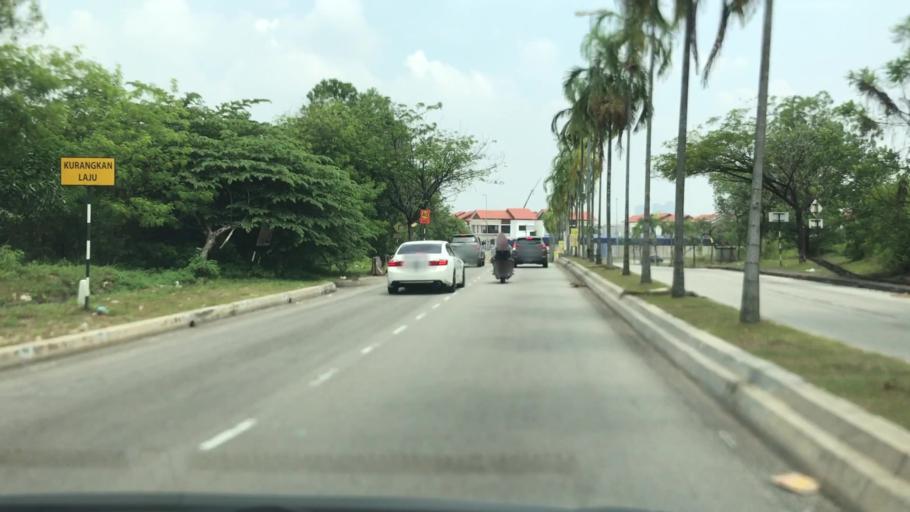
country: MY
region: Selangor
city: Kampong Baharu Balakong
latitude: 3.0402
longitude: 101.6737
